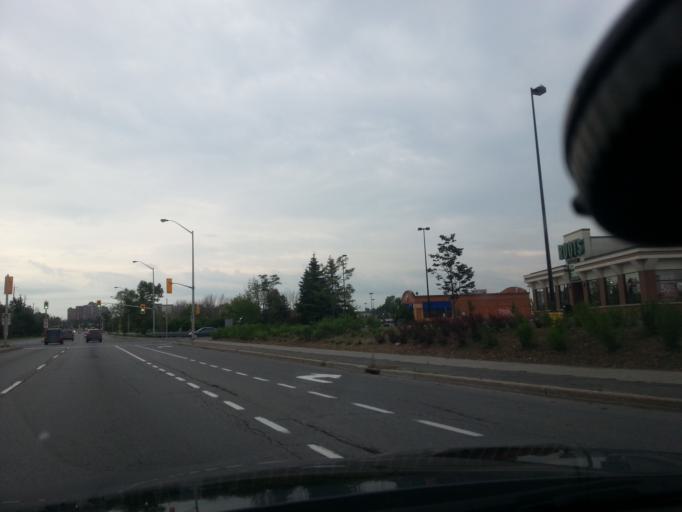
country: CA
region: Ontario
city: Ottawa
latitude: 45.3581
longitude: -75.6550
